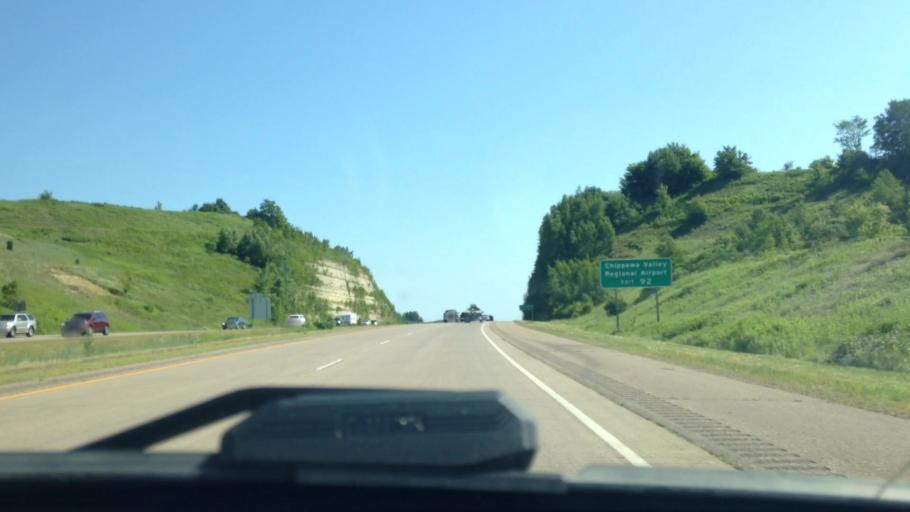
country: US
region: Wisconsin
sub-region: Eau Claire County
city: Seymour
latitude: 44.8502
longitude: -91.4373
